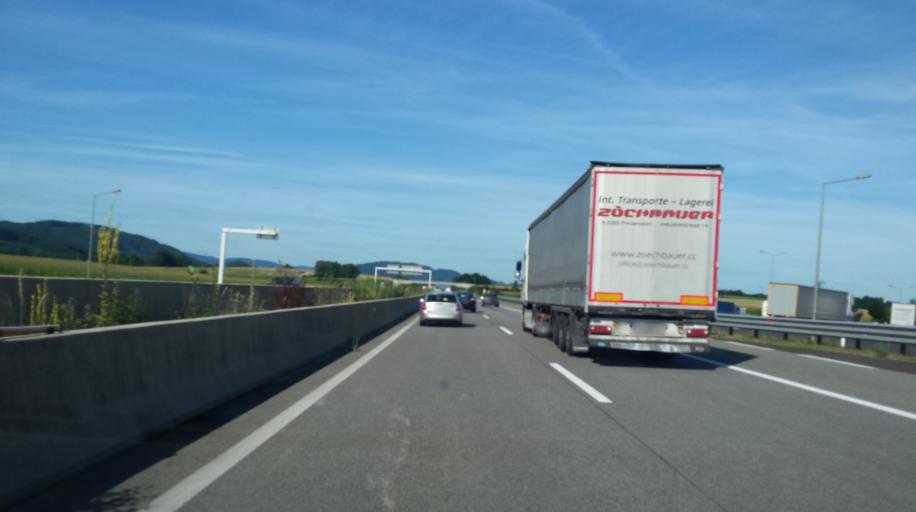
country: AT
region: Upper Austria
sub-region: Politischer Bezirk Vocklabruck
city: Aurach am Hongar
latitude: 47.9564
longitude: 13.6429
